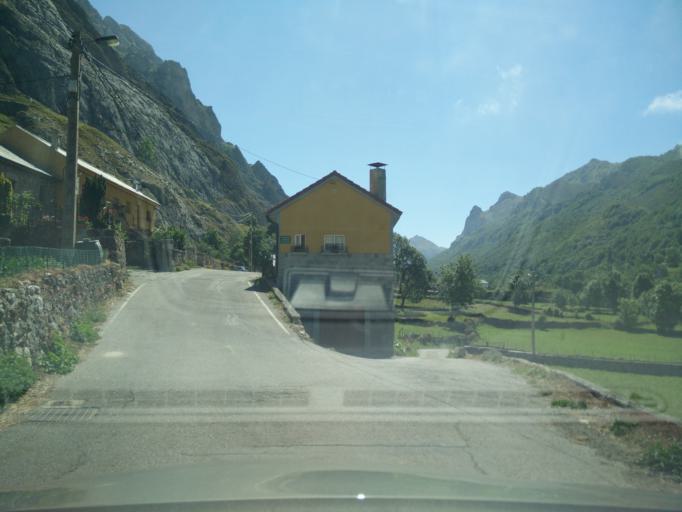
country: ES
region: Asturias
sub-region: Province of Asturias
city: Pola de Somiedo
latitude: 43.0737
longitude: -6.2031
